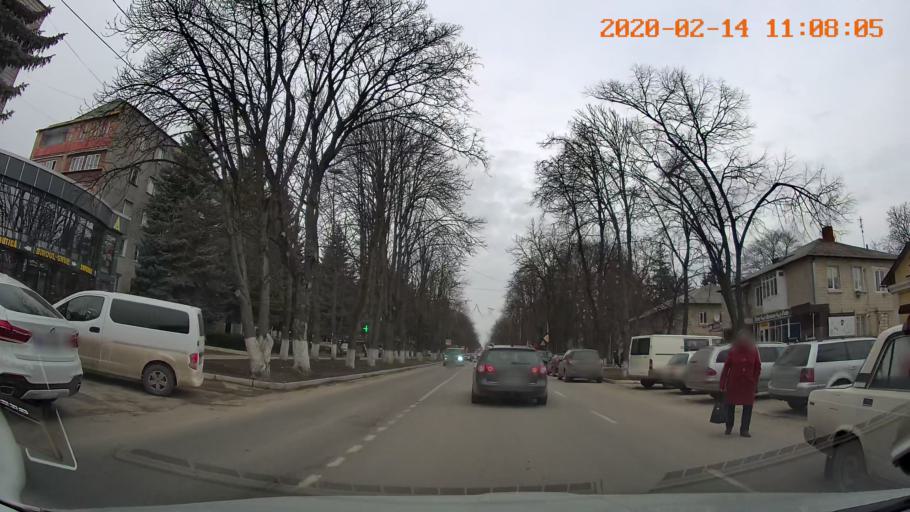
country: MD
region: Raionul Edinet
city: Edinet
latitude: 48.1706
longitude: 27.3043
